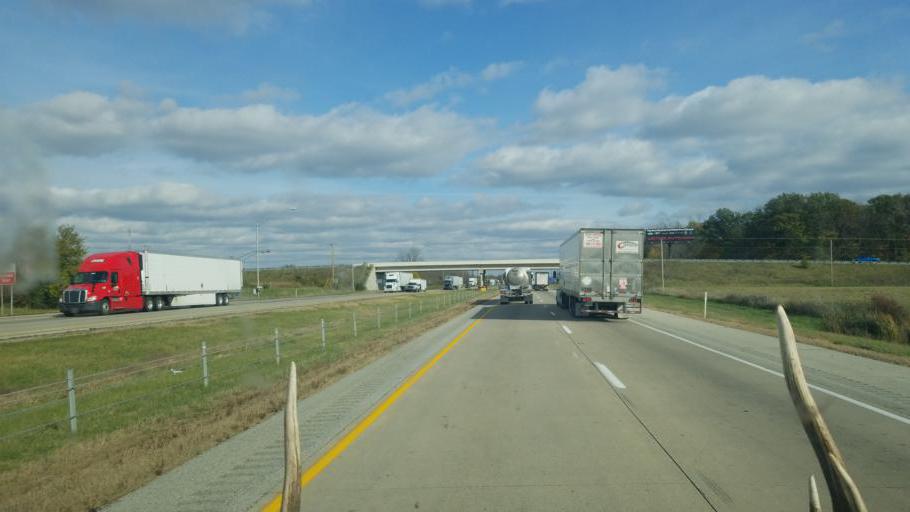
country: US
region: Indiana
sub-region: Wayne County
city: Richmond
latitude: 39.8651
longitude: -84.9413
